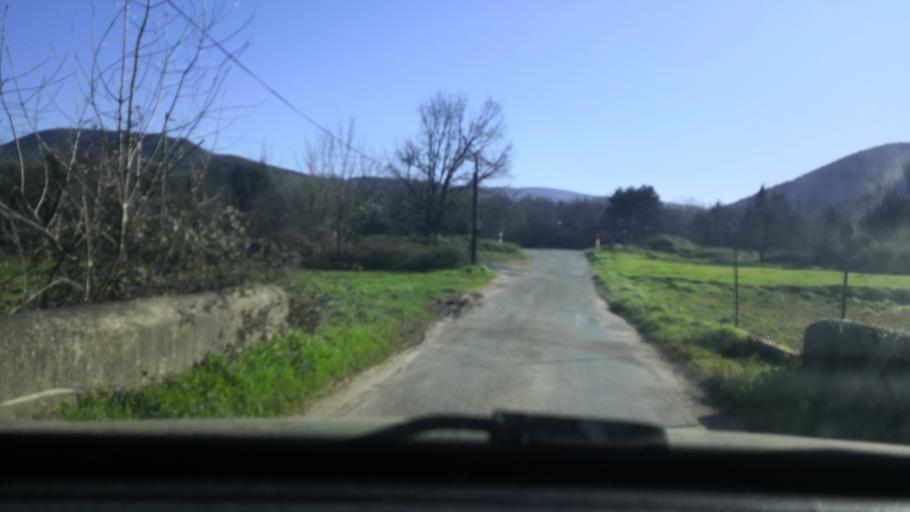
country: FR
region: Rhone-Alpes
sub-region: Departement de l'Ardeche
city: Cruas
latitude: 44.6399
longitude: 4.7893
